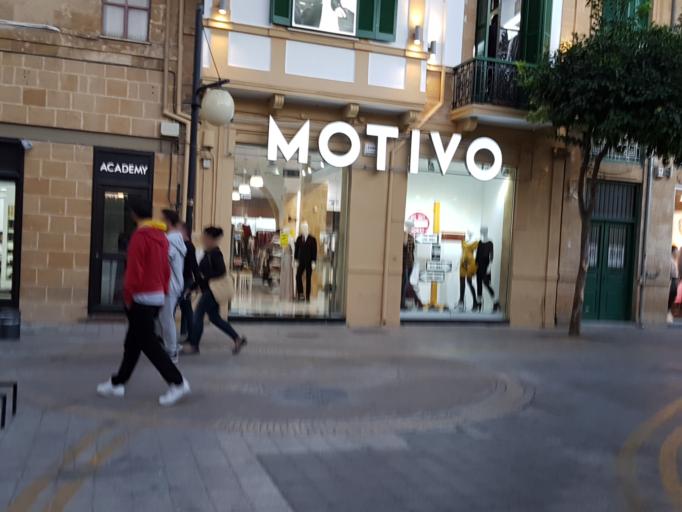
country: CY
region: Lefkosia
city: Nicosia
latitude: 35.1729
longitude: 33.3612
